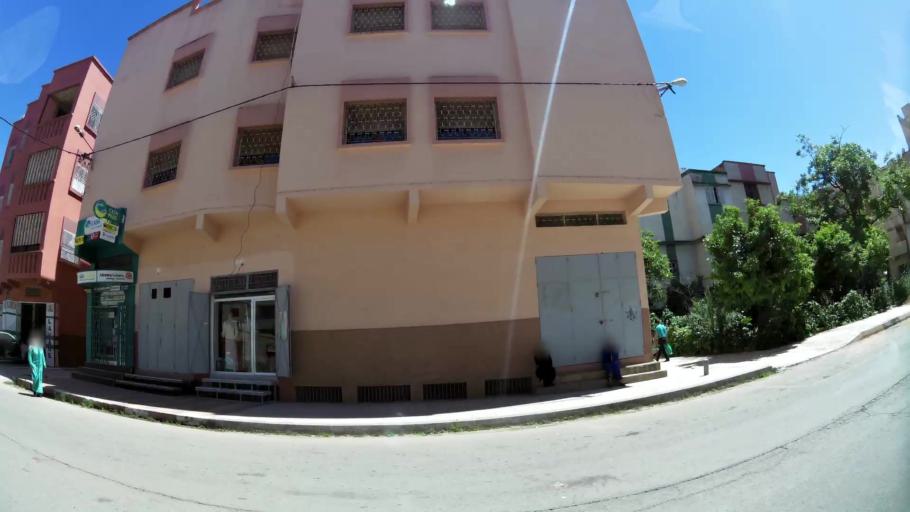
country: MA
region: Meknes-Tafilalet
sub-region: Meknes
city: Meknes
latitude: 33.8946
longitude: -5.5824
